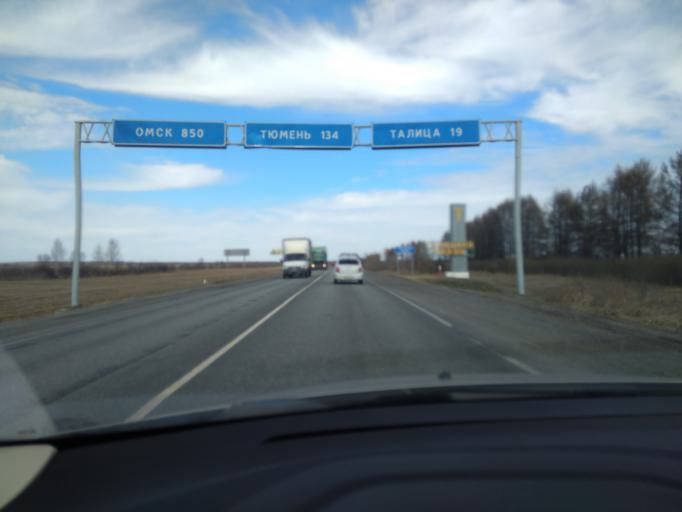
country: RU
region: Sverdlovsk
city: Pyshma
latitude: 57.0288
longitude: 63.4092
